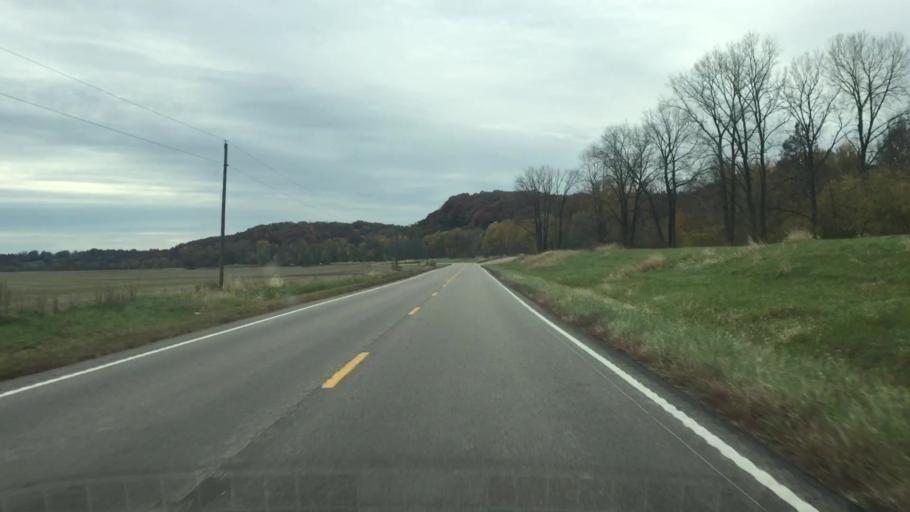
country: US
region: Missouri
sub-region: Callaway County
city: Fulton
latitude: 38.7063
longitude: -91.7793
